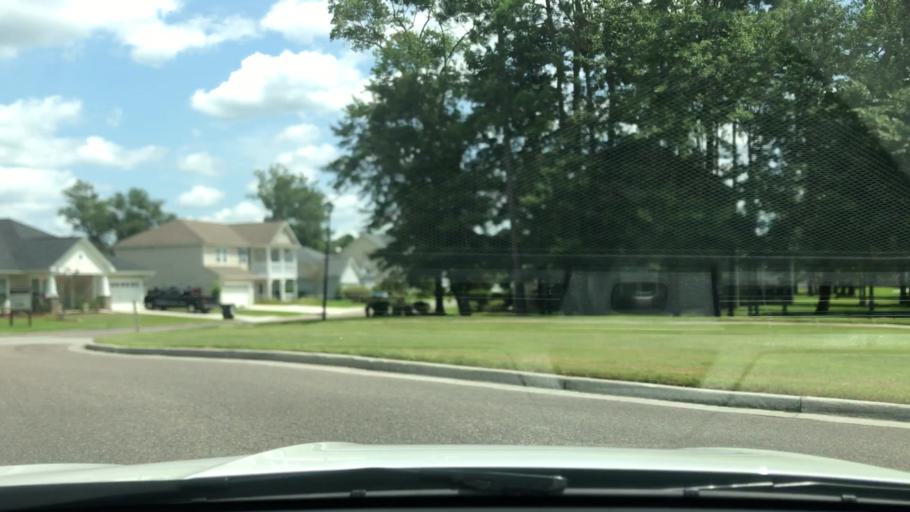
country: US
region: South Carolina
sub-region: Berkeley County
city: Moncks Corner
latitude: 33.1056
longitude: -80.0385
